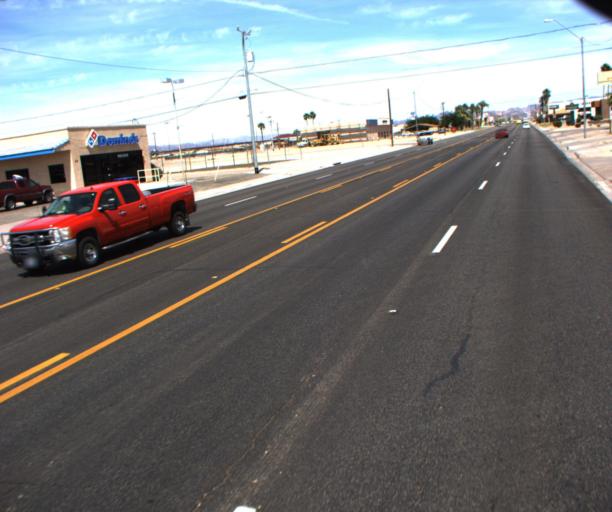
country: US
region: Arizona
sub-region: La Paz County
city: Parker
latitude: 34.1521
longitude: -114.2851
